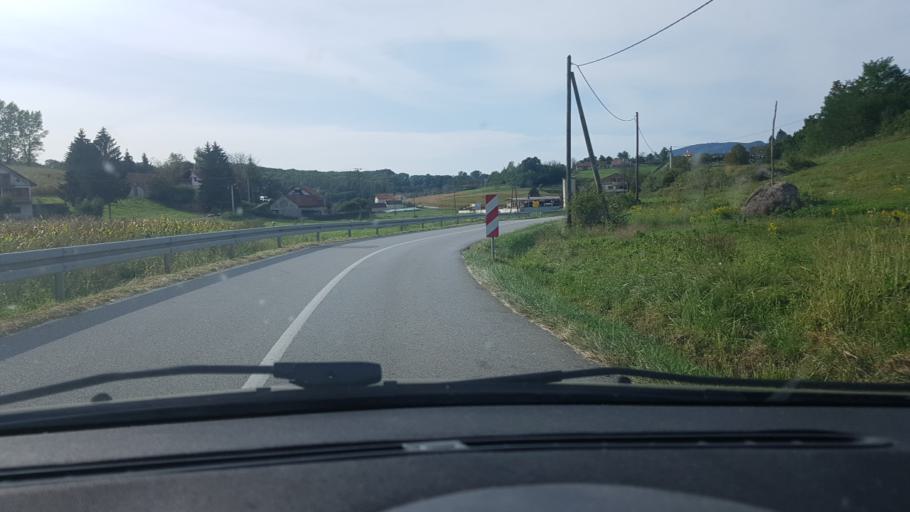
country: HR
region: Krapinsko-Zagorska
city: Mihovljan
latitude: 46.1265
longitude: 15.9790
